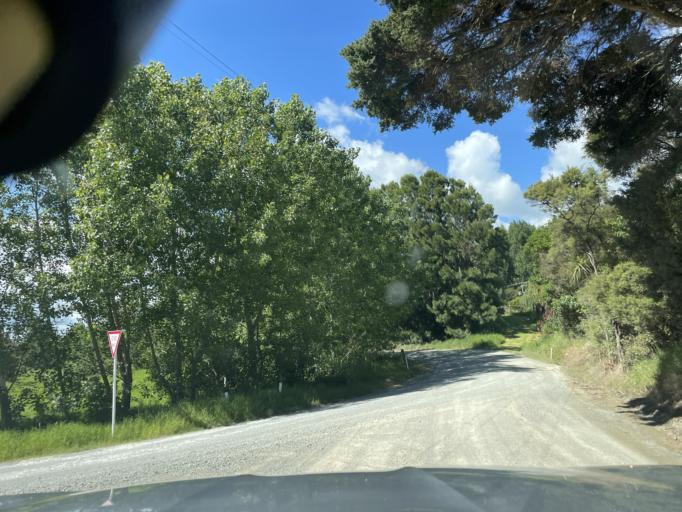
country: NZ
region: Auckland
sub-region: Auckland
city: Wellsford
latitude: -36.0836
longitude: 174.5528
